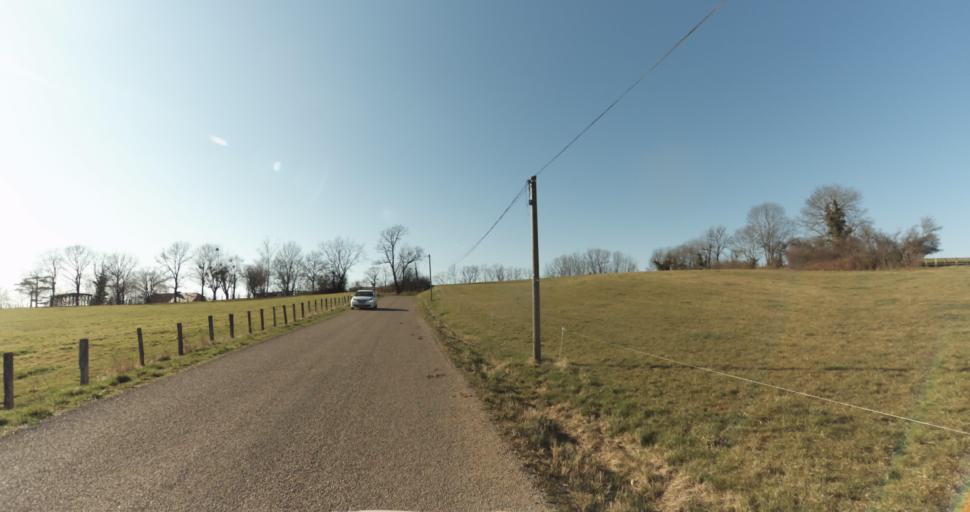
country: FR
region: Franche-Comte
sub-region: Departement du Jura
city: Montmorot
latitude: 46.6918
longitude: 5.5313
